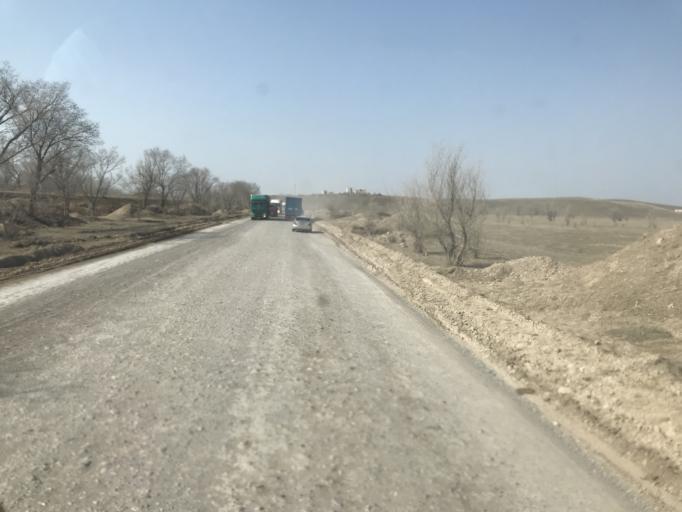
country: KG
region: Chuy
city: Bystrovka
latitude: 43.3209
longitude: 76.0070
